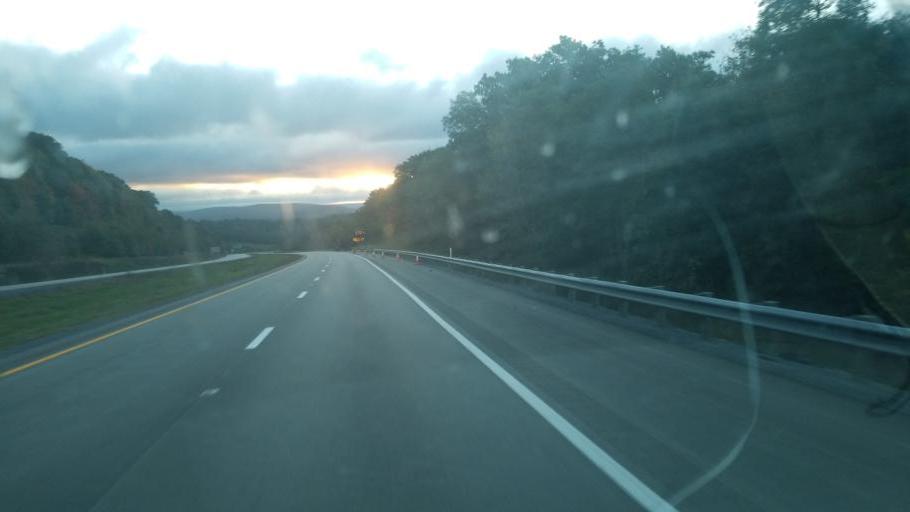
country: US
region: West Virginia
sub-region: Preston County
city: Terra Alta
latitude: 39.6629
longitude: -79.4847
